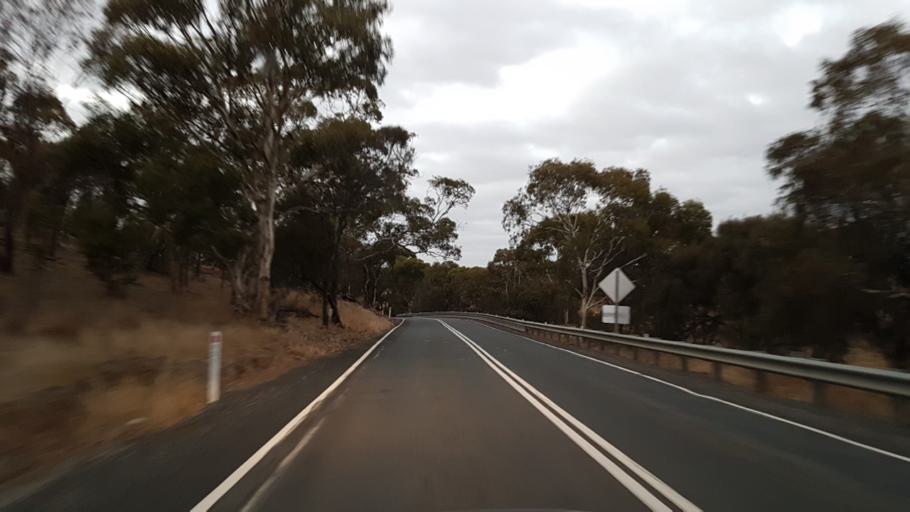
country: AU
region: South Australia
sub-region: Mount Barker
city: Callington
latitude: -35.0506
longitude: 139.0014
